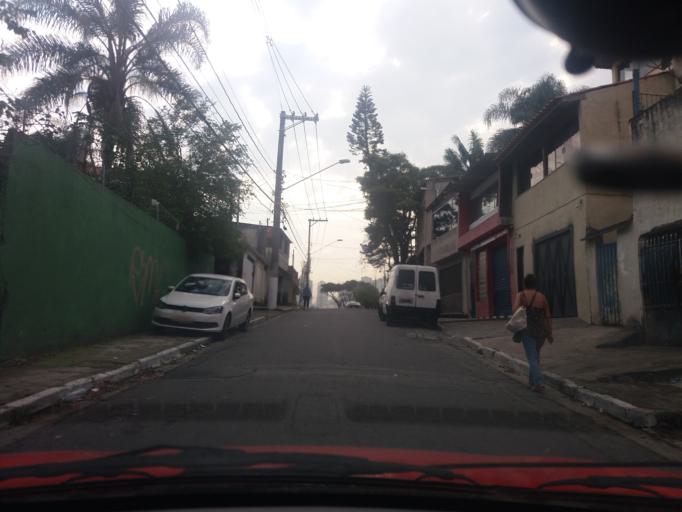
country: BR
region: Sao Paulo
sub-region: Taboao Da Serra
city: Taboao da Serra
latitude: -23.6145
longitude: -46.7461
